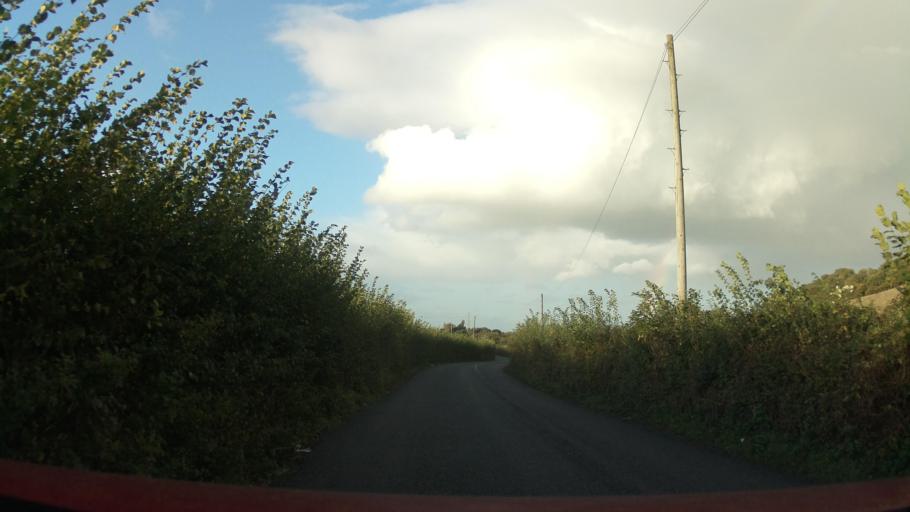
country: GB
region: England
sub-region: South Gloucestershire
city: Severn Beach
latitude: 51.5282
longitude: -2.6369
